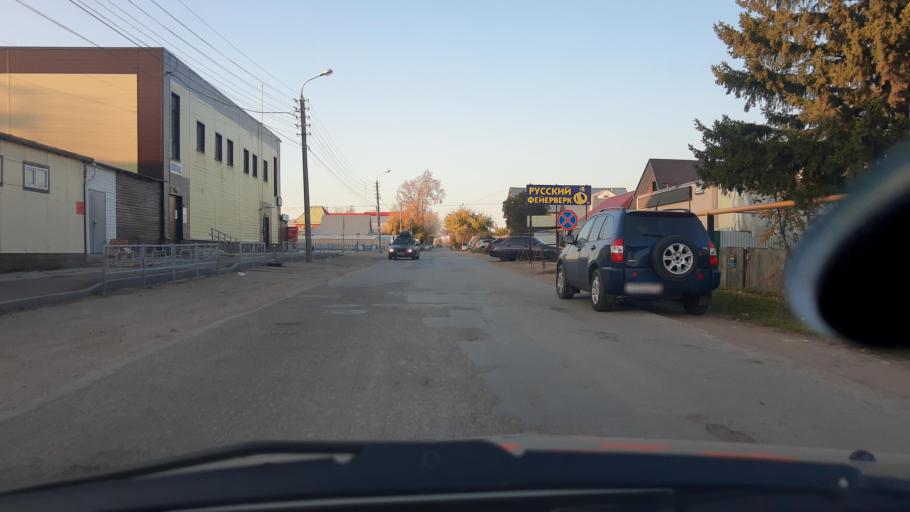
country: RU
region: Bashkortostan
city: Mikhaylovka
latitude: 54.6939
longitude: 55.8493
